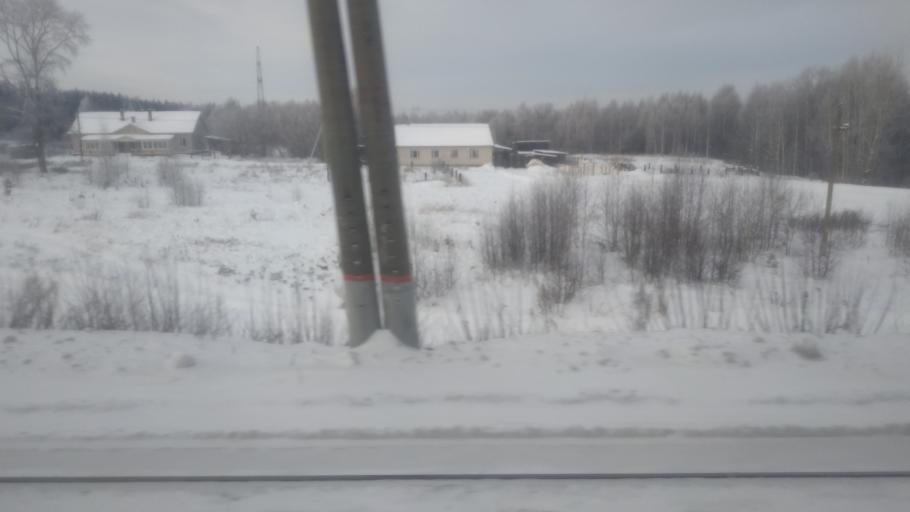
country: RU
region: Udmurtiya
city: Kizner
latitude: 56.3887
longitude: 51.7212
